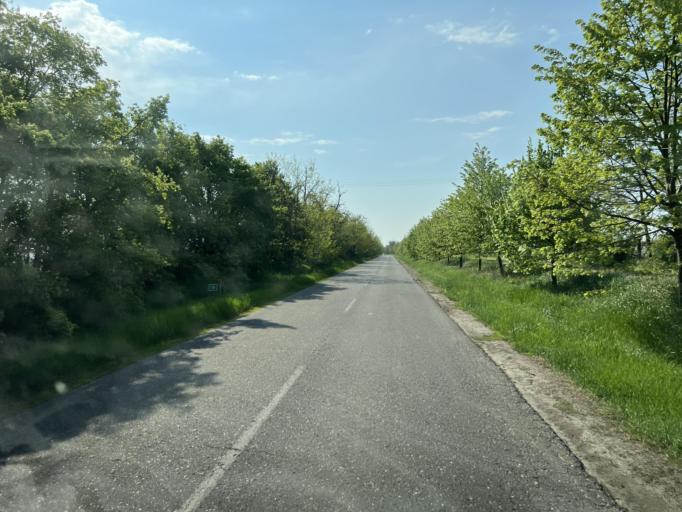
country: HU
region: Pest
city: Jaszkarajeno
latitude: 47.0921
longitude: 20.0274
